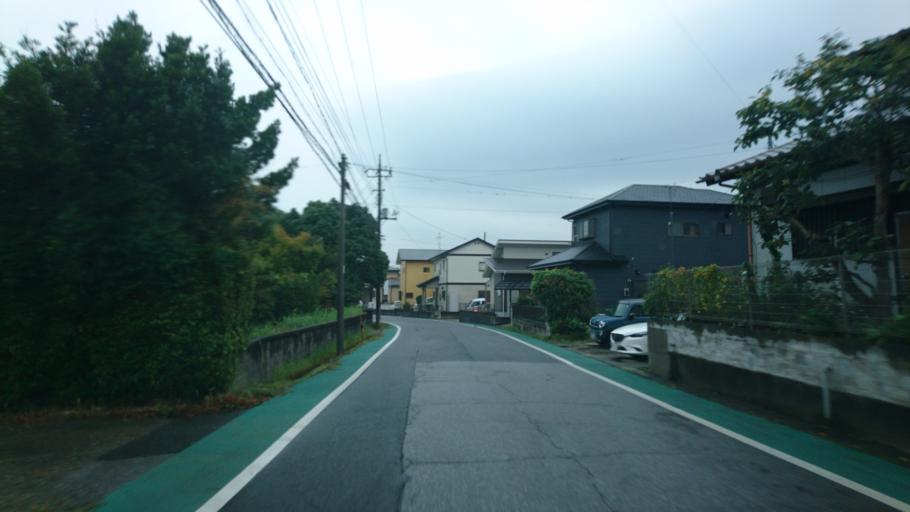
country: JP
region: Chiba
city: Kimitsu
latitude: 35.3039
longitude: 139.9504
